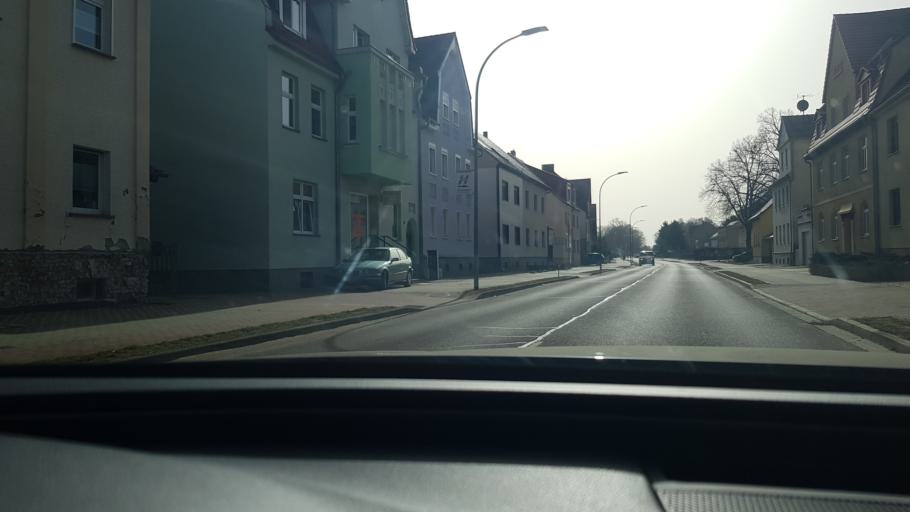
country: DE
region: Brandenburg
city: Guben
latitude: 51.9626
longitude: 14.7022
